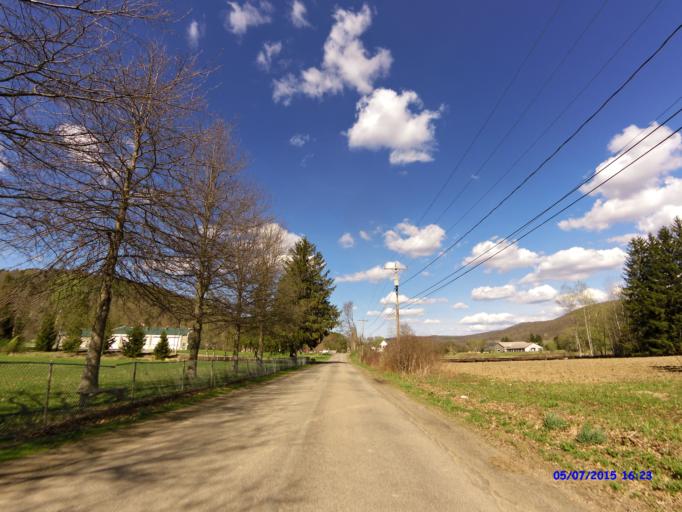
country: US
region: New York
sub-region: Cattaraugus County
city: Salamanca
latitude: 42.2819
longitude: -78.6717
